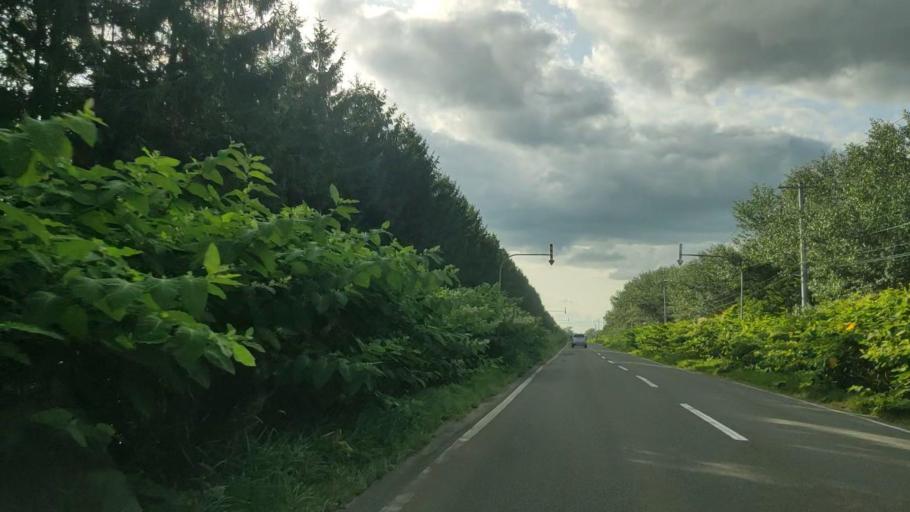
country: JP
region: Hokkaido
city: Makubetsu
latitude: 44.8998
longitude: 141.9128
